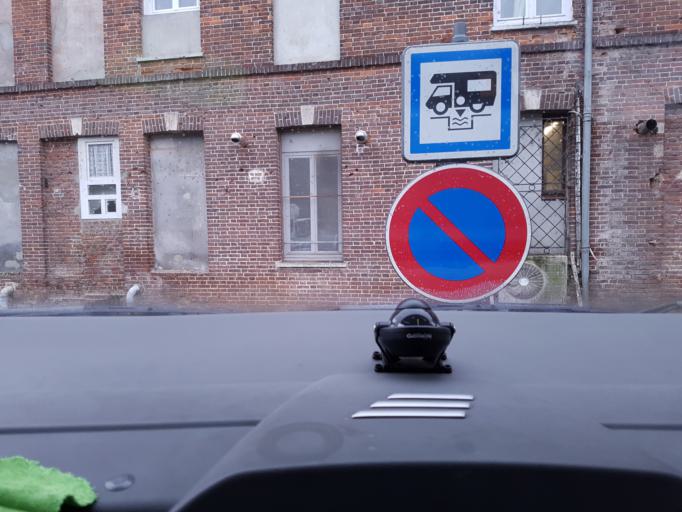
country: FR
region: Haute-Normandie
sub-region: Departement de l'Eure
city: Beaumont-le-Roger
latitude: 49.0807
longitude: 0.7778
